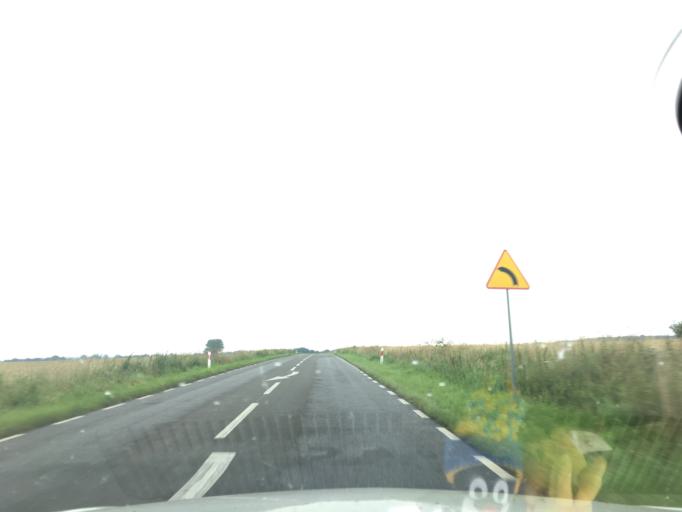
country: PL
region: West Pomeranian Voivodeship
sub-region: Powiat gryficki
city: Karnice
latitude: 54.0520
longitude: 15.0763
